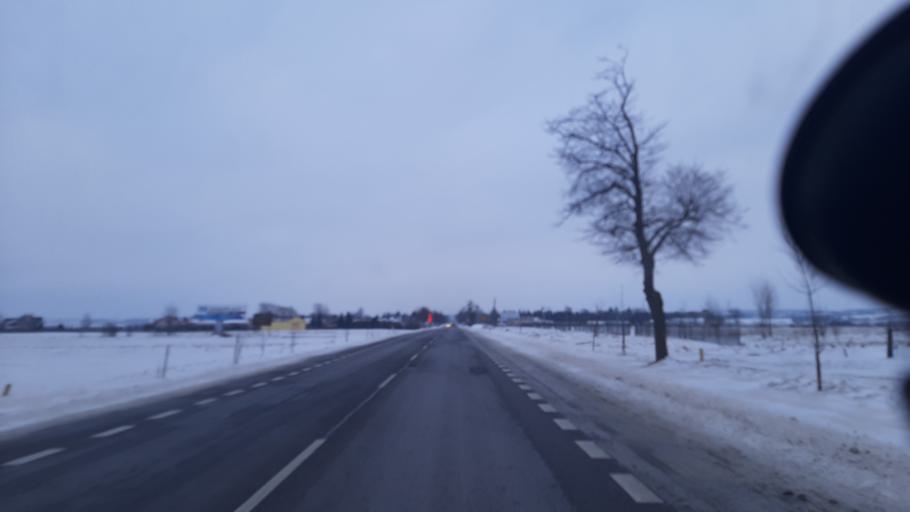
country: PL
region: Lublin Voivodeship
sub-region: Powiat pulawski
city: Markuszow
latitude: 51.3792
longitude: 22.2399
